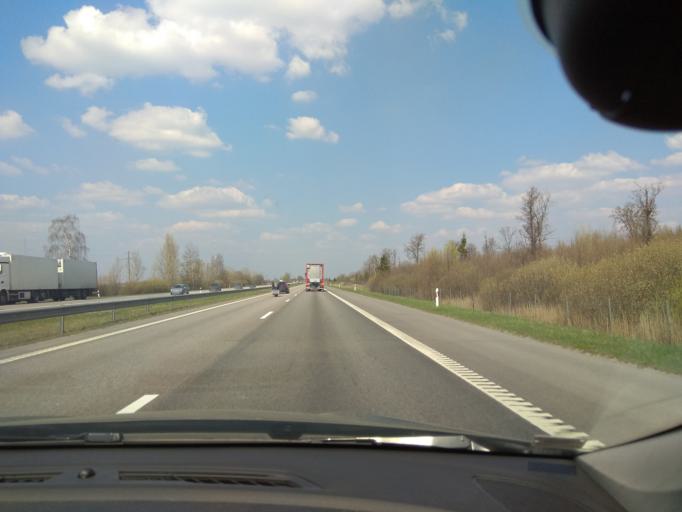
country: LT
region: Kauno apskritis
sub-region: Kaunas
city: Sargenai
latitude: 55.0198
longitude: 23.8330
